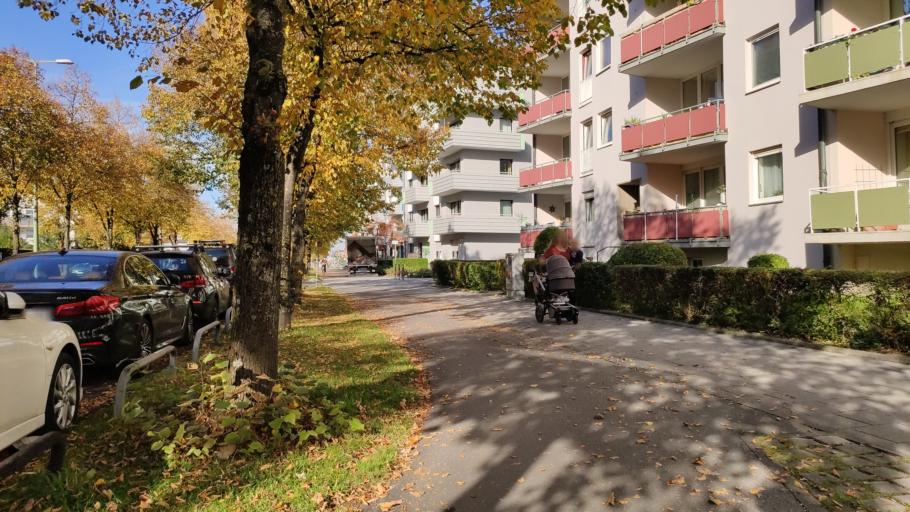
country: DE
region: Bavaria
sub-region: Upper Bavaria
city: Neuried
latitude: 48.1141
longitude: 11.4771
